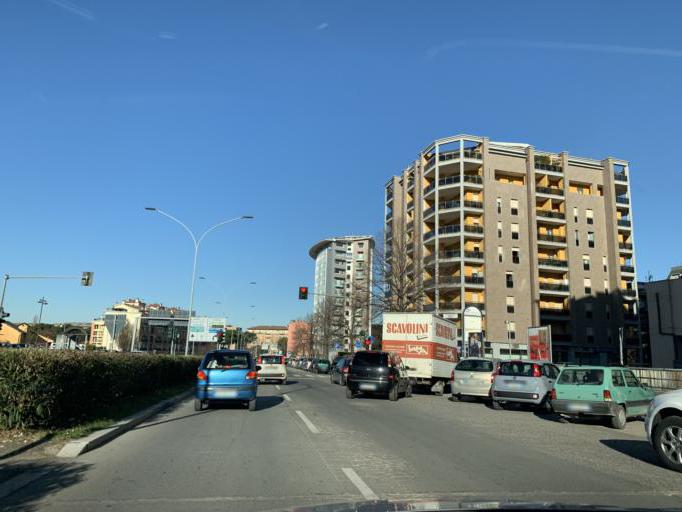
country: IT
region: Umbria
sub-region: Provincia di Terni
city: Terni
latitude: 42.5594
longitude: 12.6550
